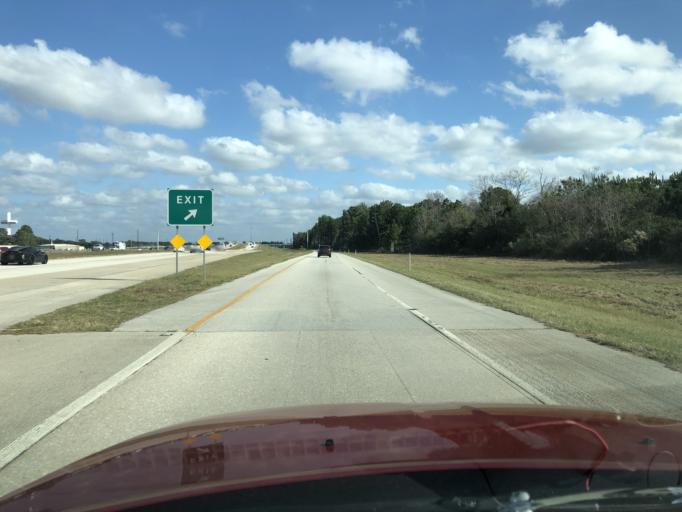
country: US
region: Texas
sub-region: Harris County
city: Tomball
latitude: 30.0519
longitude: -95.6286
